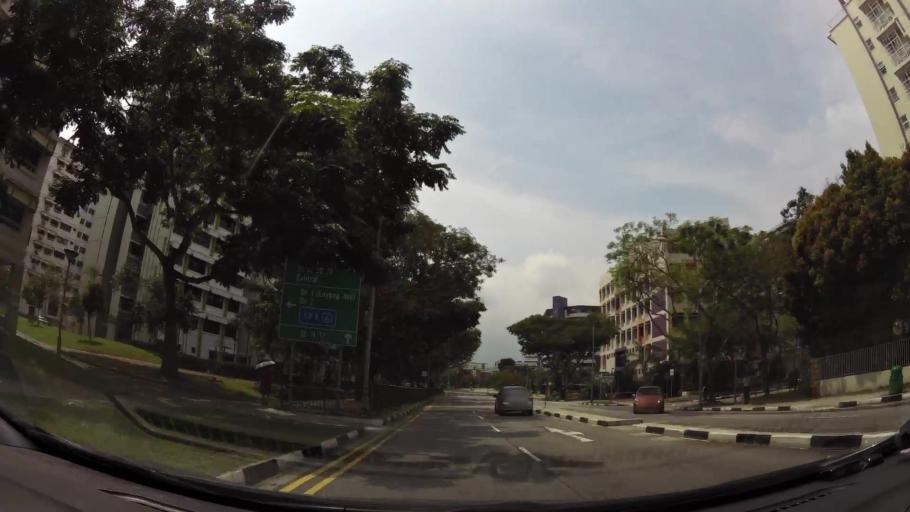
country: MY
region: Johor
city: Kampung Pasir Gudang Baru
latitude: 1.3688
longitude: 103.9601
